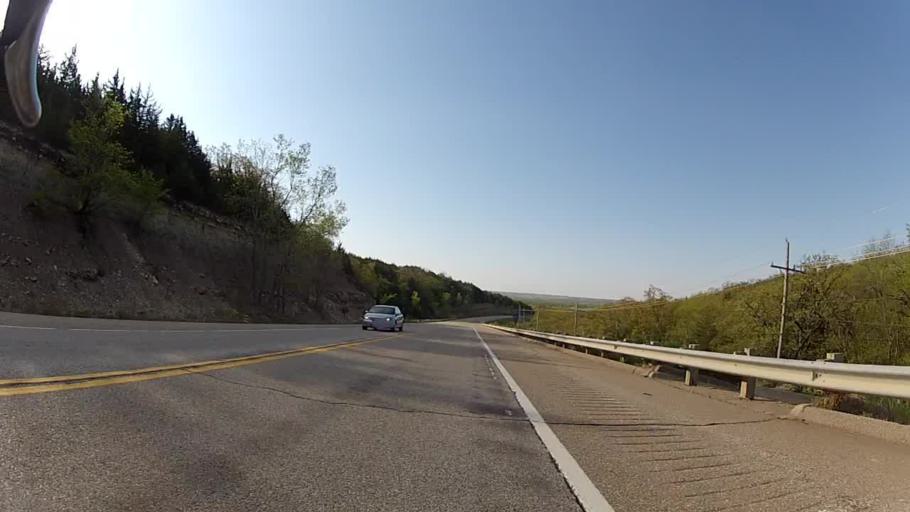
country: US
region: Kansas
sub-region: Riley County
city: Manhattan
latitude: 39.1730
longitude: -96.6457
